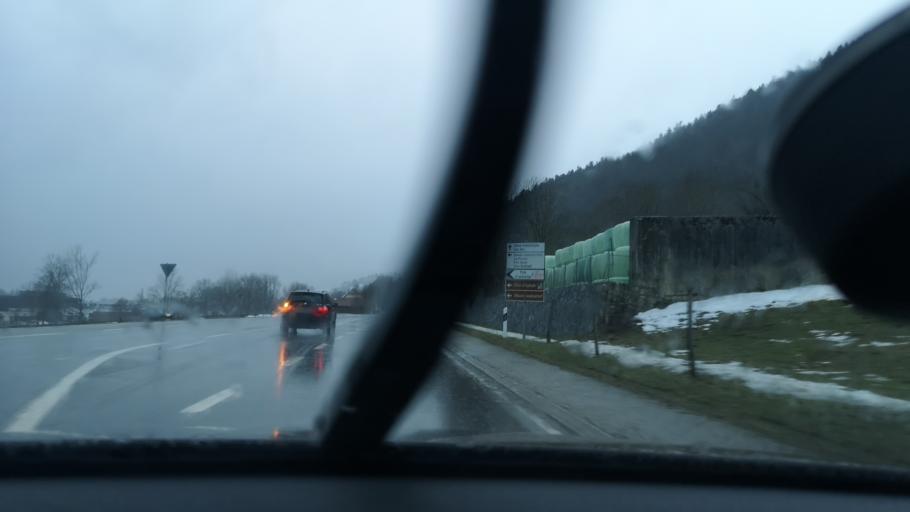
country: CH
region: Neuchatel
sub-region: Val-de-Travers District
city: Couvet
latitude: 46.9337
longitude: 6.6527
